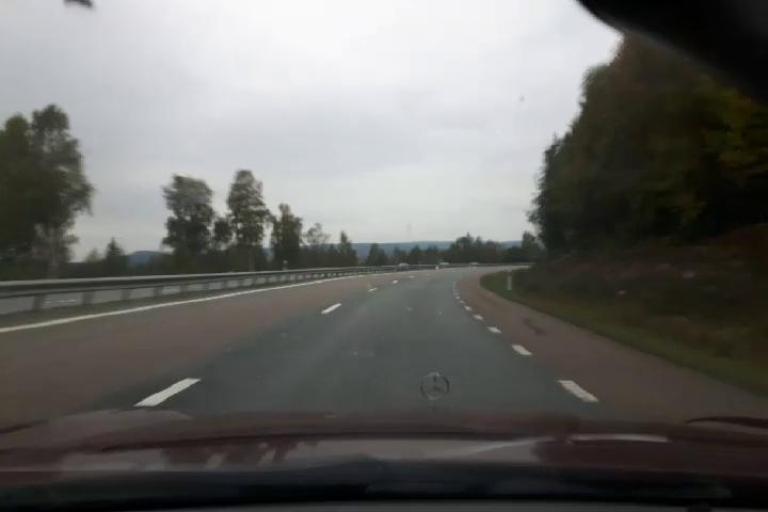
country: SE
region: Vaesternorrland
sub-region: Kramfors Kommun
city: Nordingra
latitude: 63.0077
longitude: 18.2791
